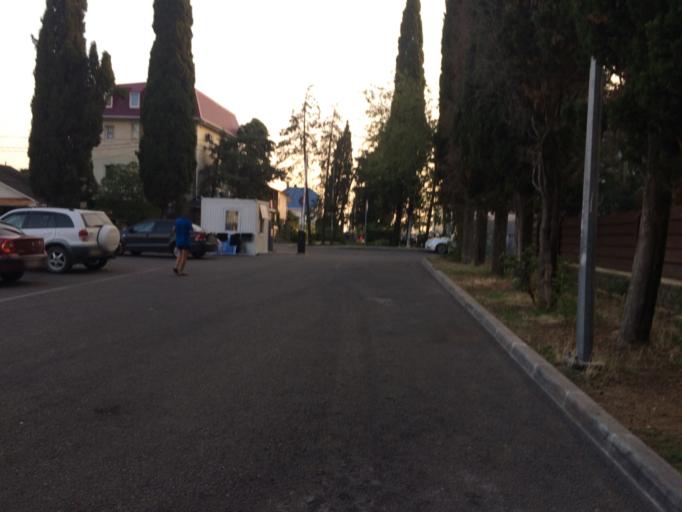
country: RU
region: Krasnodarskiy
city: Adler
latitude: 43.3898
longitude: 39.9871
